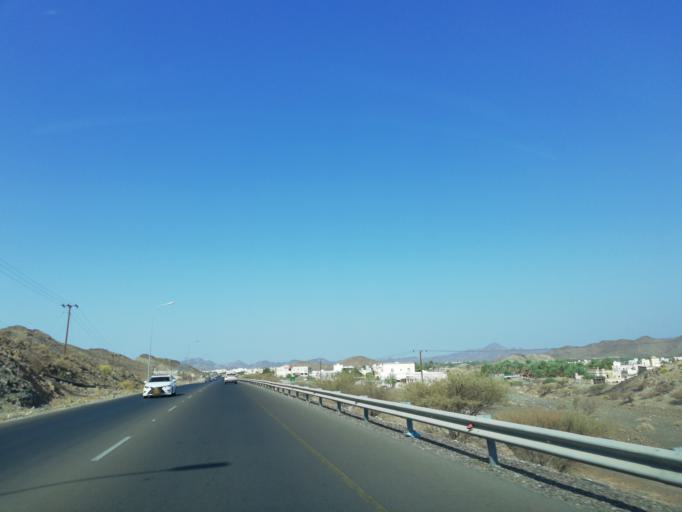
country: OM
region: Ash Sharqiyah
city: Ibra'
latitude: 22.8039
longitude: 58.1647
